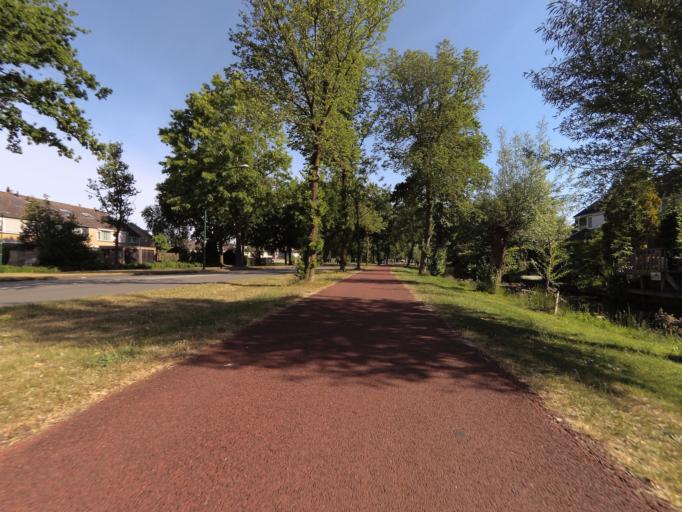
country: NL
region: Utrecht
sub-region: Gemeente Bunschoten
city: Spakenburg
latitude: 52.2448
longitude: 5.3678
